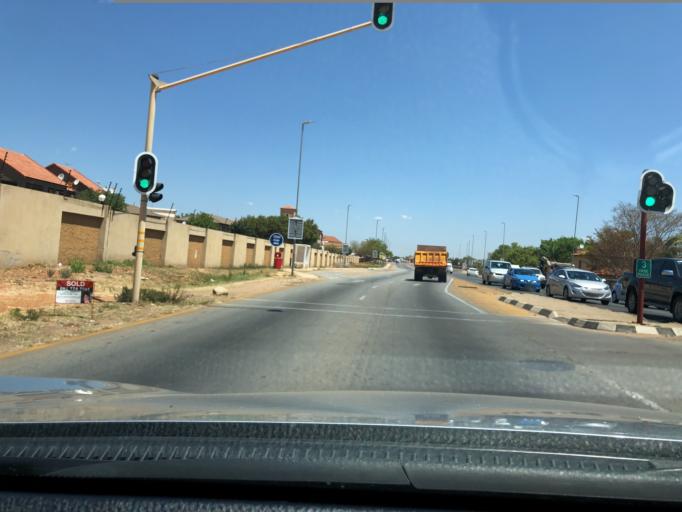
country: ZA
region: Limpopo
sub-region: Capricorn District Municipality
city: Polokwane
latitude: -23.8806
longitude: 29.5033
